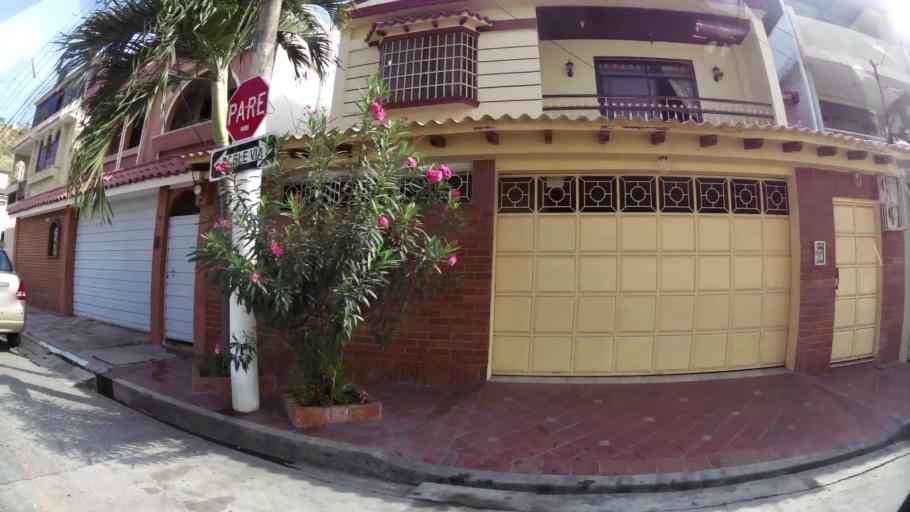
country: EC
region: Guayas
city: Guayaquil
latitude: -2.1842
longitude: -79.9105
